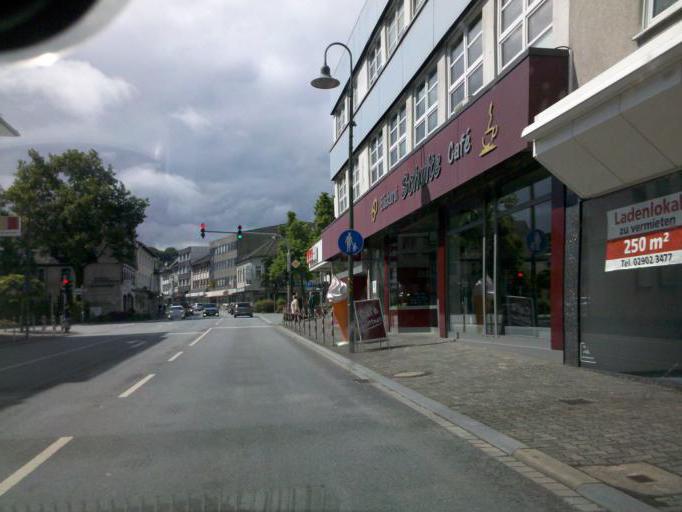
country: DE
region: North Rhine-Westphalia
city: Warstein
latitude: 51.4449
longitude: 8.3542
